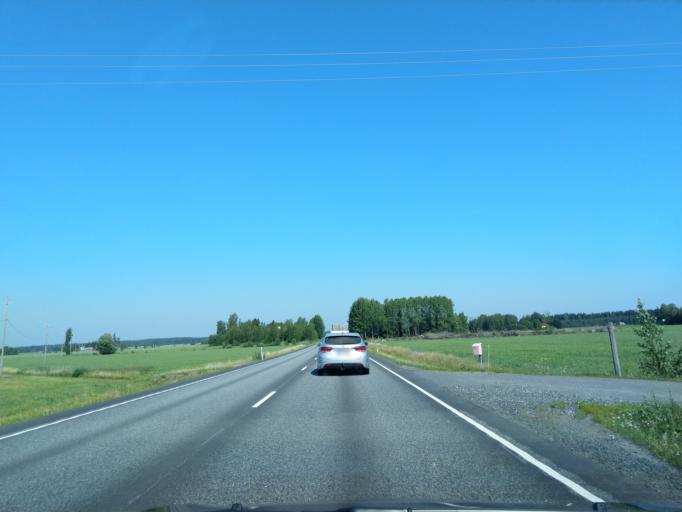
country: FI
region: Varsinais-Suomi
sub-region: Loimaa
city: Alastaro
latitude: 61.0845
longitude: 22.8956
